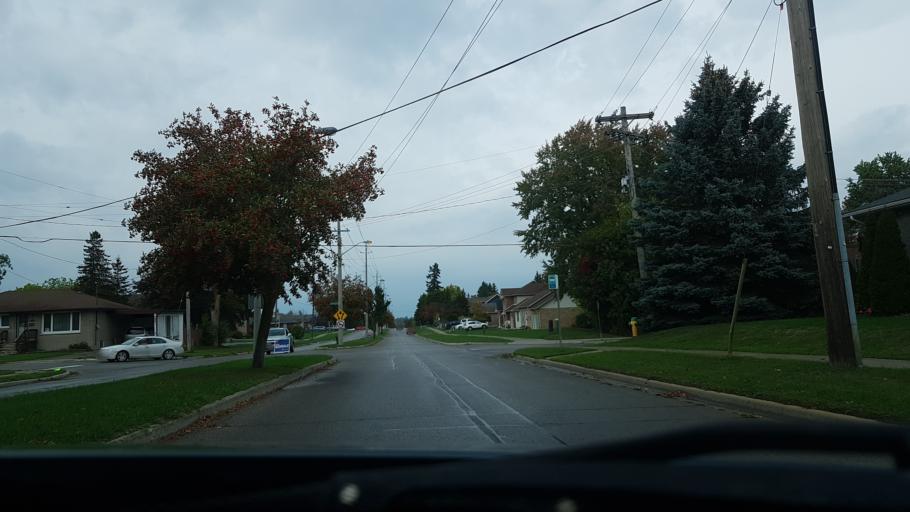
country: CA
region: Ontario
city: Omemee
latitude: 44.3630
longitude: -78.7449
